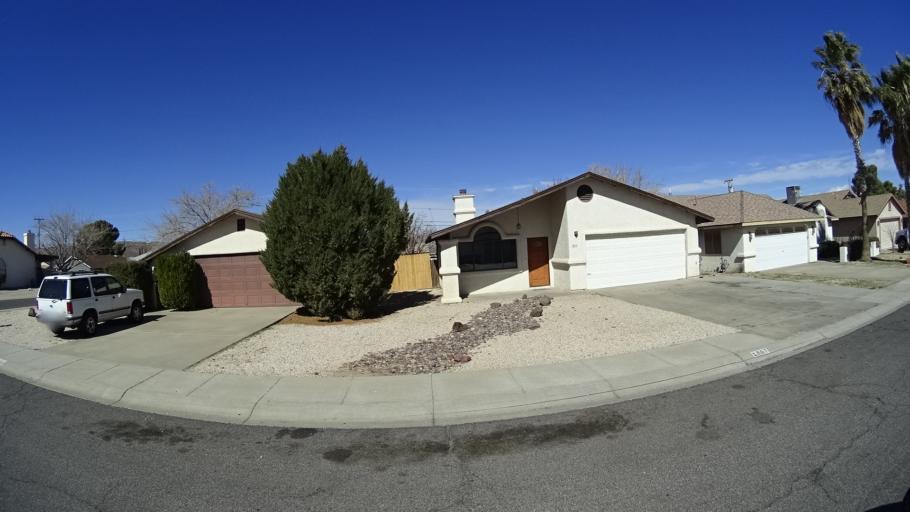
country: US
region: Arizona
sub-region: Mohave County
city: Kingman
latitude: 35.2067
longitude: -114.0377
